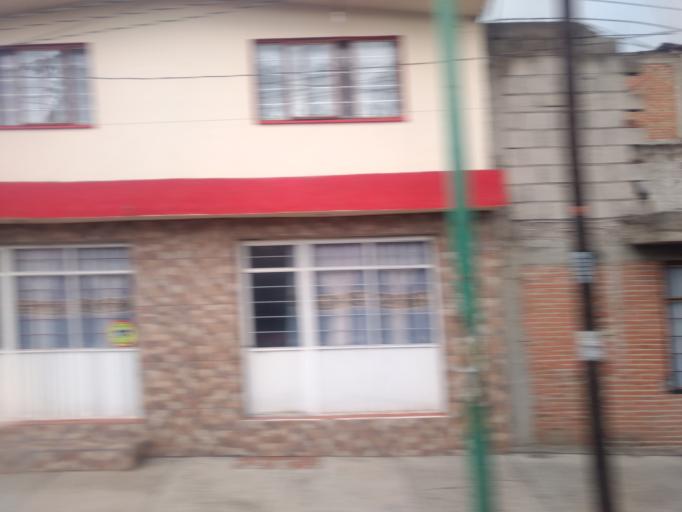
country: MX
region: Tlaxcala
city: Apizaco
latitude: 19.4159
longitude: -98.1502
